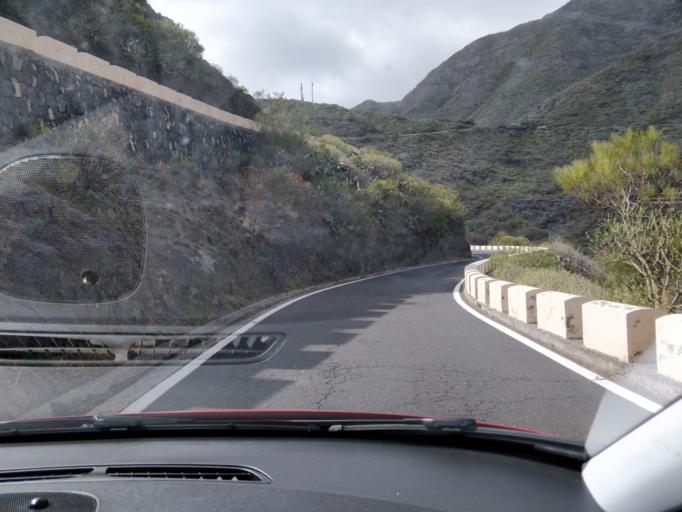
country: ES
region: Canary Islands
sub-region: Provincia de Santa Cruz de Tenerife
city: Santiago del Teide
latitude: 28.3086
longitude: -16.8458
